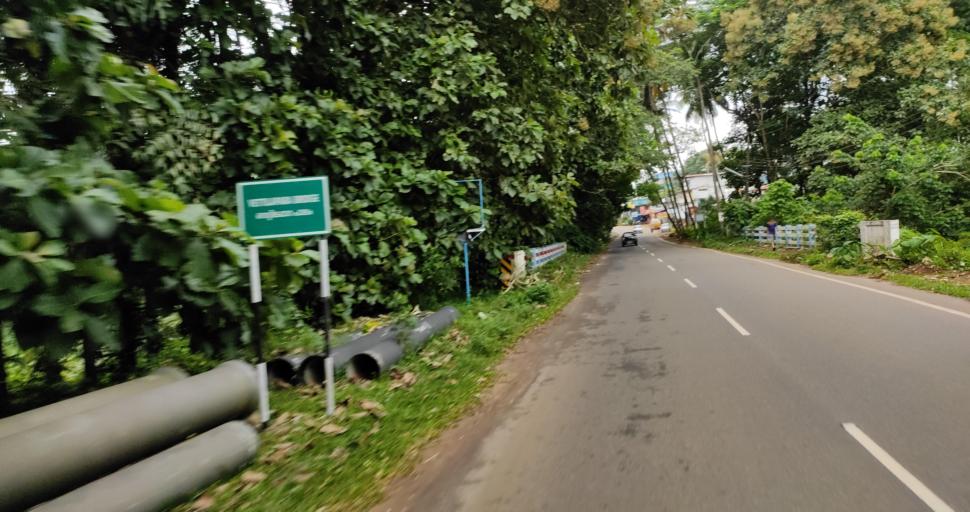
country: IN
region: Kerala
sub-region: Ernakulam
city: Angamali
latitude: 10.2951
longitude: 76.4907
